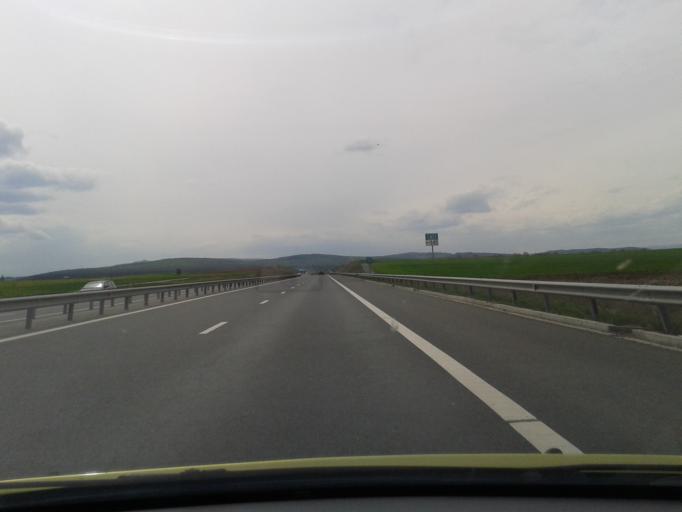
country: RO
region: Hunedoara
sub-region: Comuna Turdas
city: Pricaz
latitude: 45.8575
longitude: 23.1443
